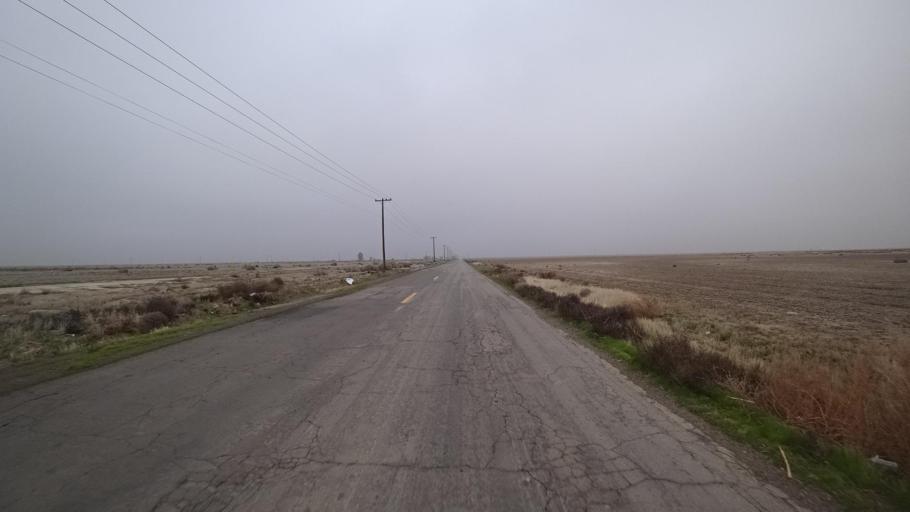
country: US
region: California
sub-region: Tulare County
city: Alpaugh
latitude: 35.7174
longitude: -119.4716
